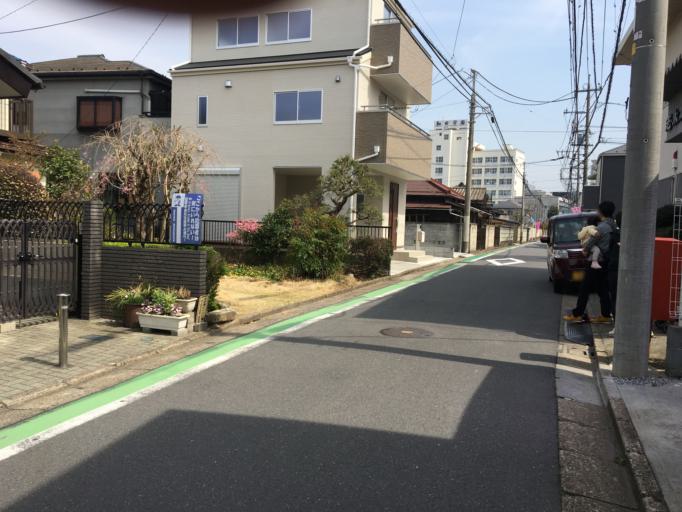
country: JP
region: Saitama
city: Shiki
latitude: 35.8325
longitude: 139.5797
